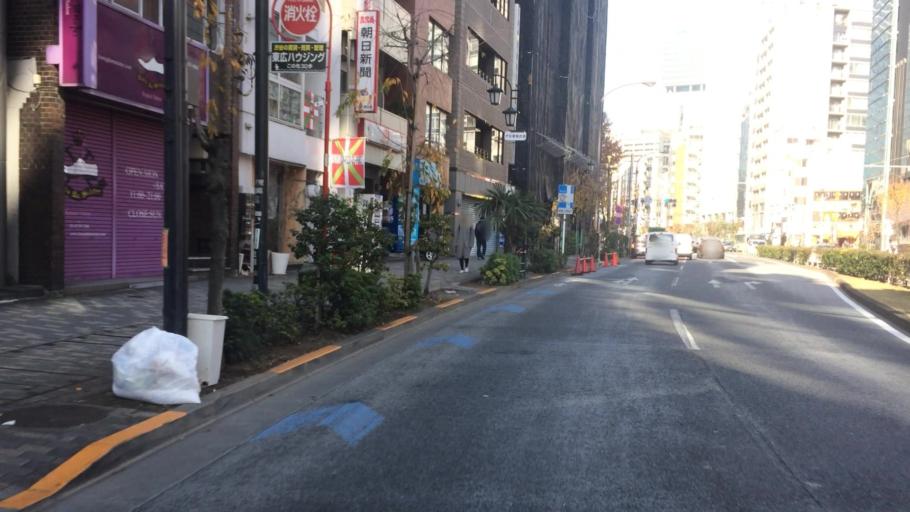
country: JP
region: Tokyo
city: Tokyo
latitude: 35.6544
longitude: 139.7074
